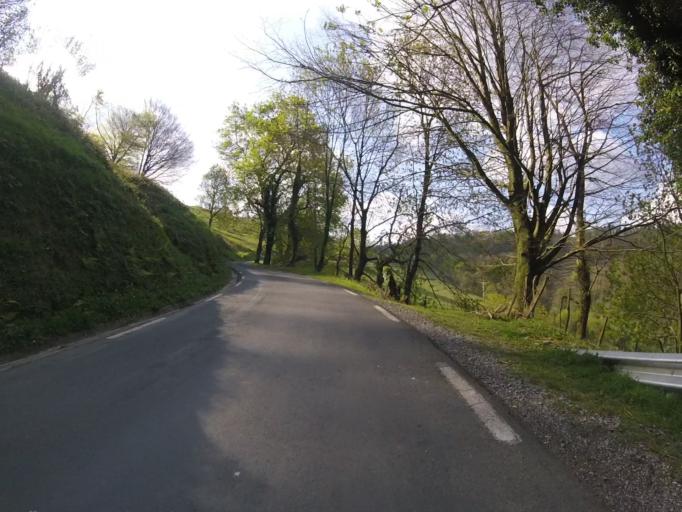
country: ES
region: Basque Country
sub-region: Provincia de Guipuzcoa
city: Azkoitia
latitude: 43.2224
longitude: -2.3117
